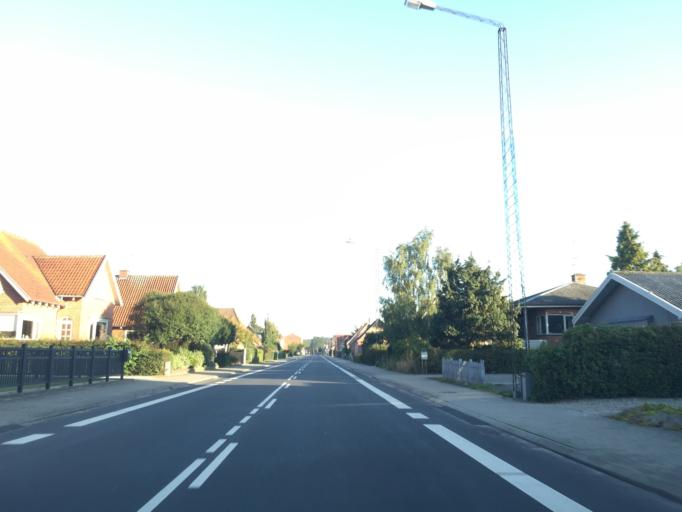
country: DK
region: Central Jutland
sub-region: Viborg Kommune
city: Bjerringbro
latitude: 56.3665
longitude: 9.6630
